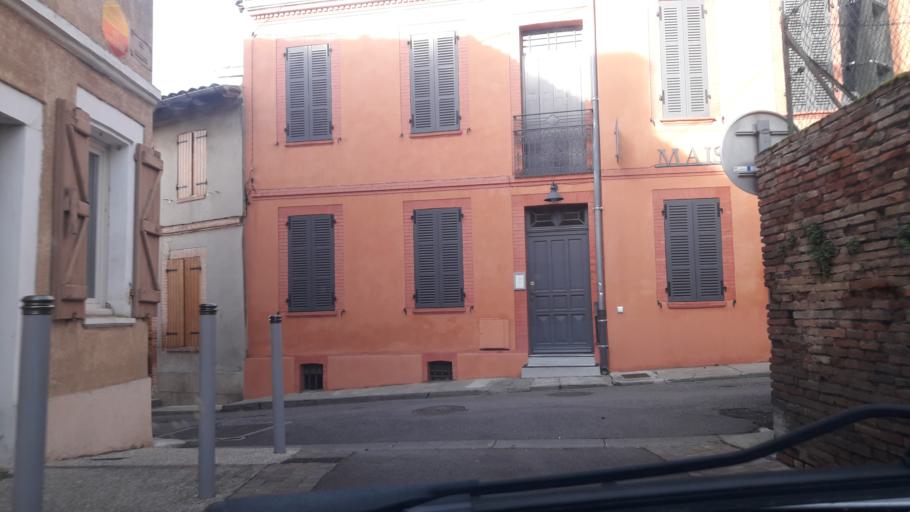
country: FR
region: Midi-Pyrenees
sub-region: Departement du Gers
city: Pujaudran
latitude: 43.6145
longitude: 1.0802
